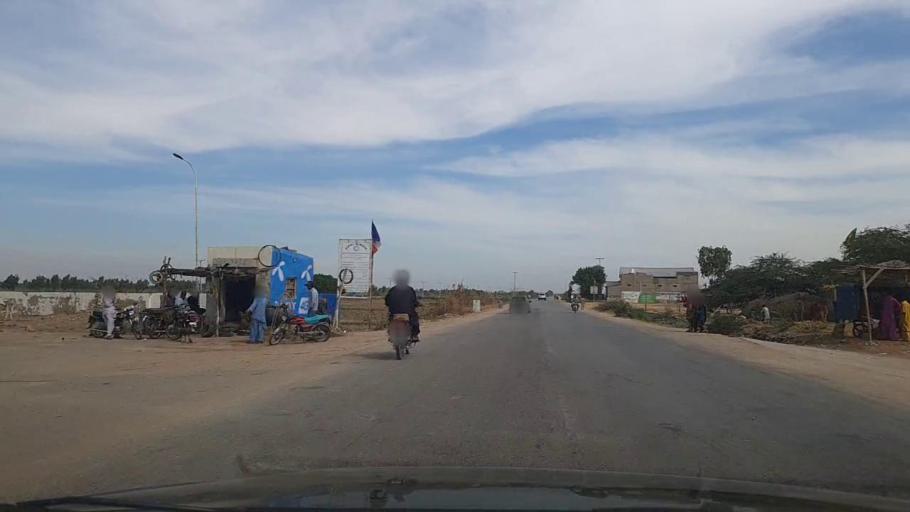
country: PK
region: Sindh
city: Thatta
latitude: 24.7948
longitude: 67.9597
